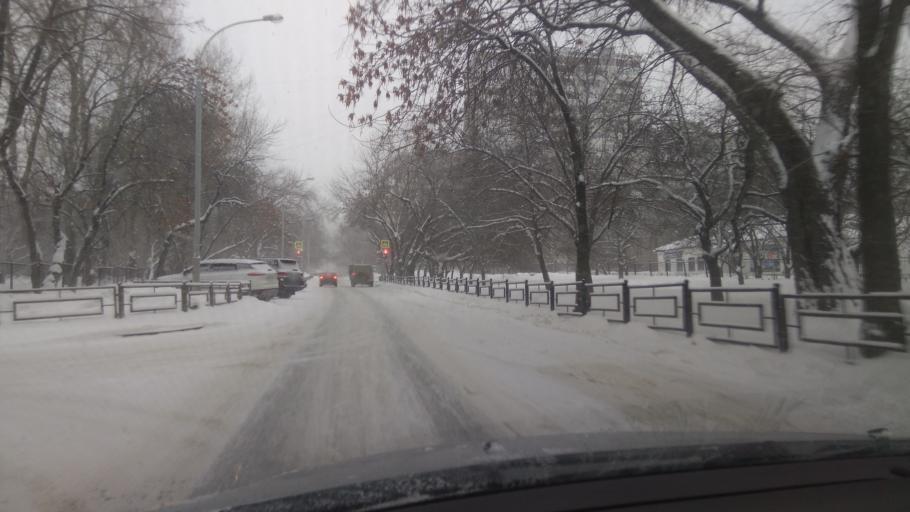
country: RU
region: Sverdlovsk
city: Yekaterinburg
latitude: 56.8206
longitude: 60.6314
